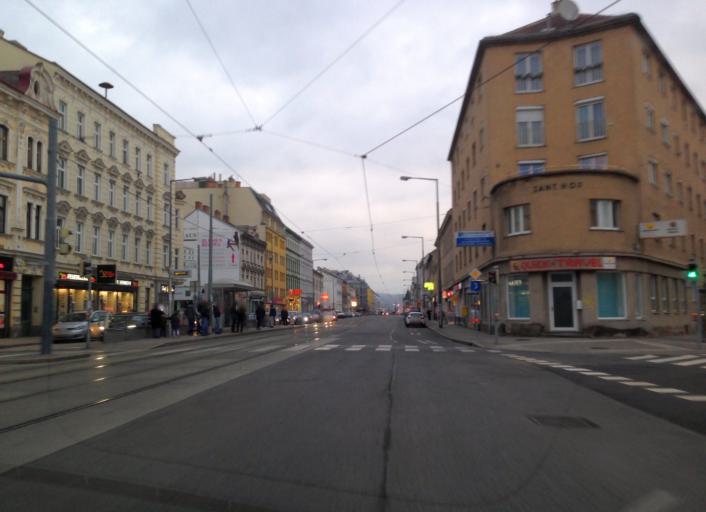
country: AT
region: Lower Austria
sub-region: Politischer Bezirk Korneuburg
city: Langenzersdorf
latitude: 48.2659
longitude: 16.3934
